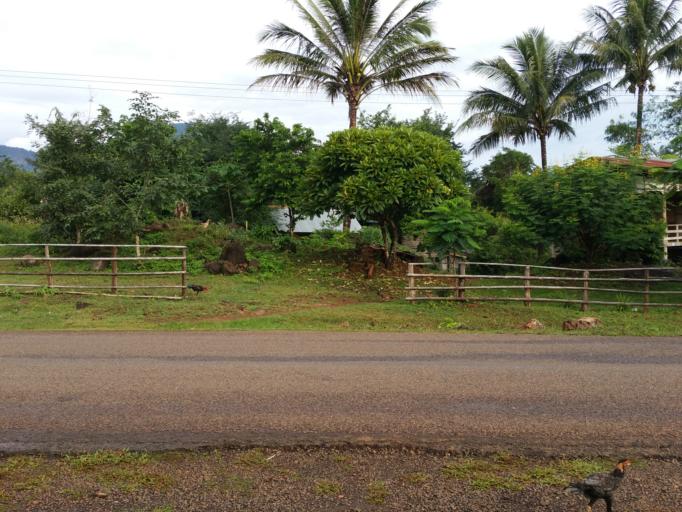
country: LA
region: Champasak
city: Pakxe
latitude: 15.3455
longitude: 105.9854
